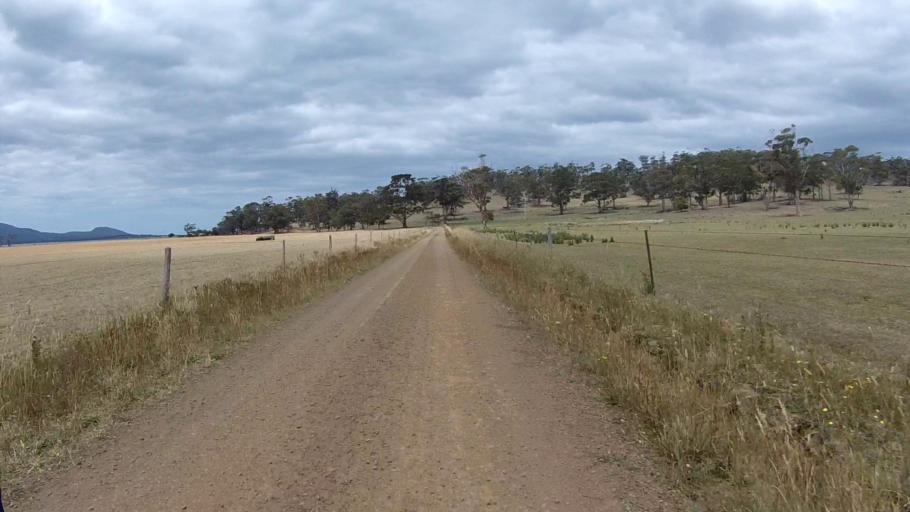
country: AU
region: Tasmania
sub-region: Sorell
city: Sorell
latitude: -42.6608
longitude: 147.9440
